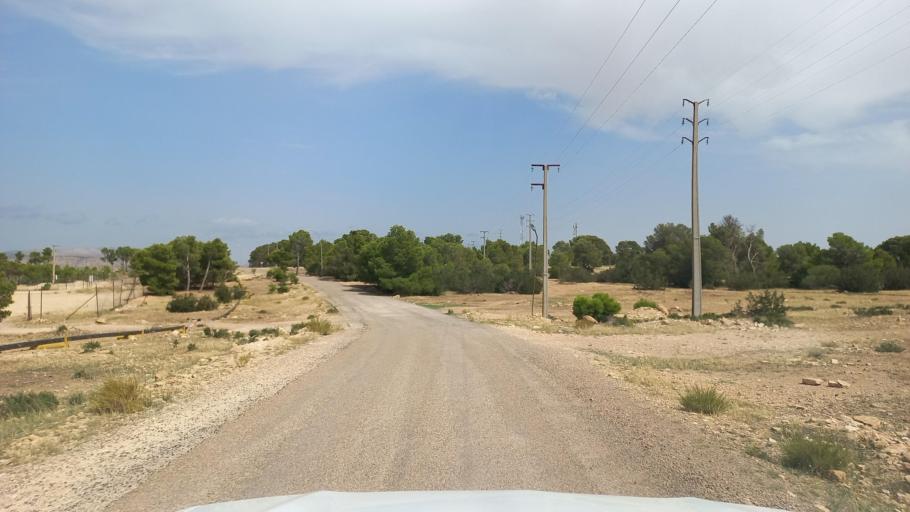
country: TN
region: Al Qasrayn
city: Kasserine
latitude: 35.3834
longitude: 8.8987
